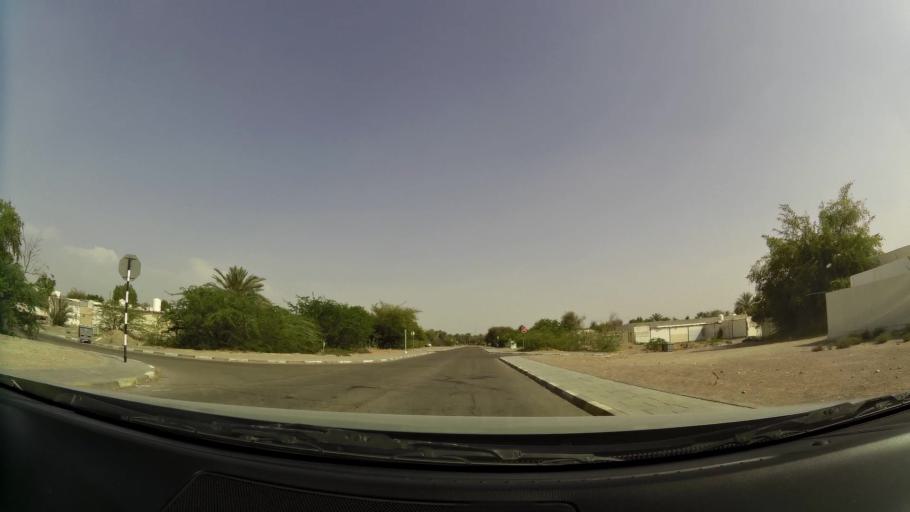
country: AE
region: Abu Dhabi
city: Al Ain
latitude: 24.2356
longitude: 55.7031
